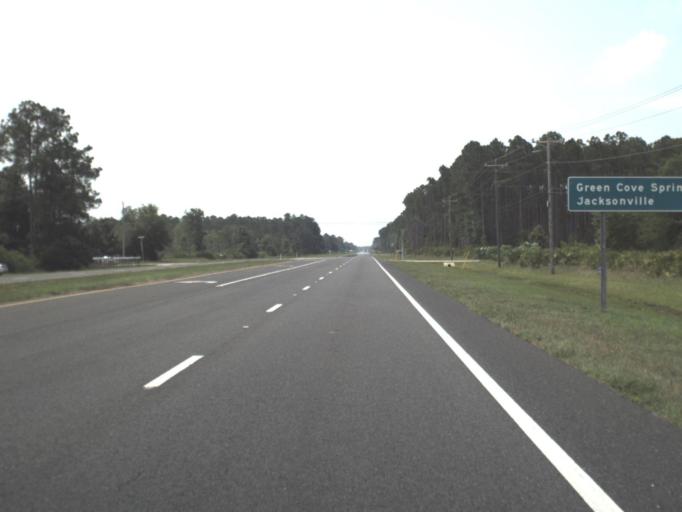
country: US
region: Florida
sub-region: Clay County
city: Green Cove Springs
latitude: 29.8421
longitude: -81.6618
